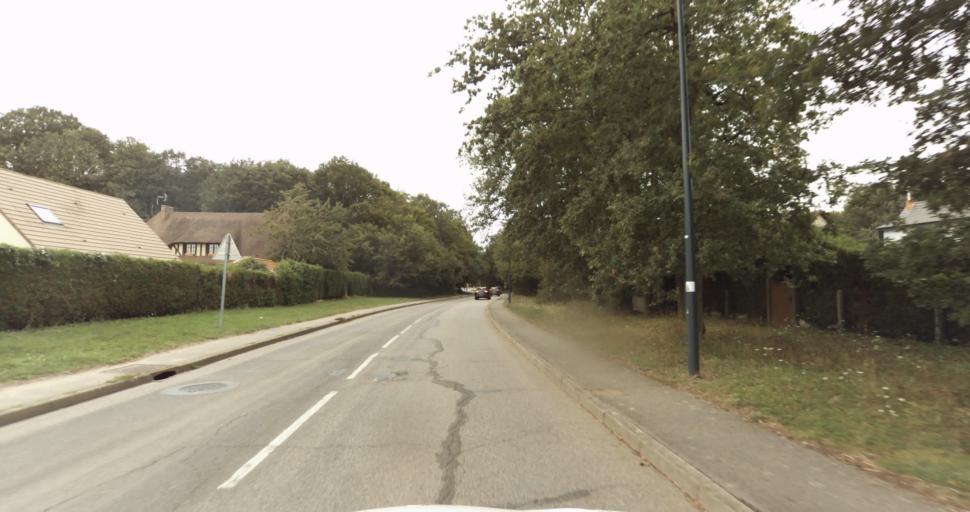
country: FR
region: Haute-Normandie
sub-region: Departement de l'Eure
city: Gravigny
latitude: 49.0327
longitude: 1.1775
